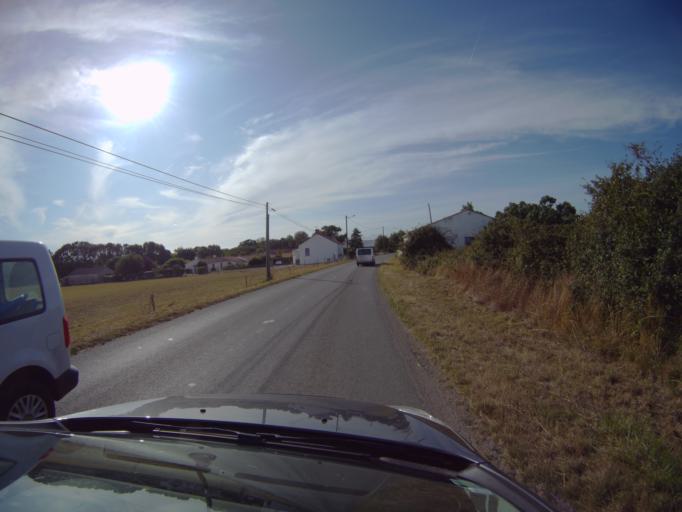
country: FR
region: Pays de la Loire
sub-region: Departement de la Vendee
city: Angles
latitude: 46.4112
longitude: -1.4510
